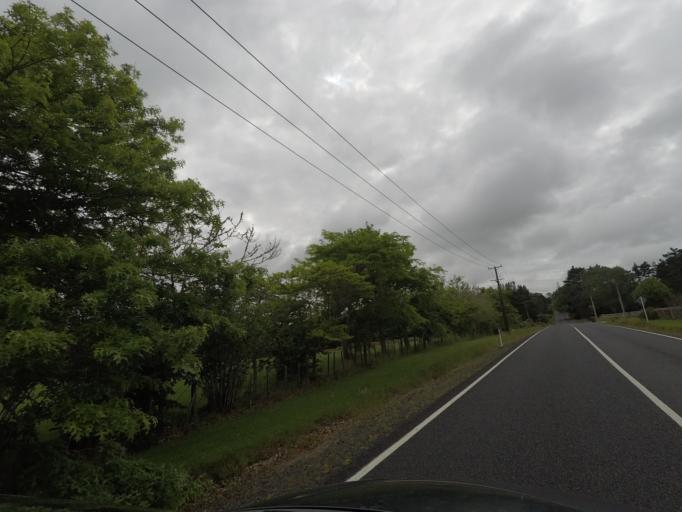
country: NZ
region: Auckland
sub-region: Auckland
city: Muriwai Beach
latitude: -36.8187
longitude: 174.5641
